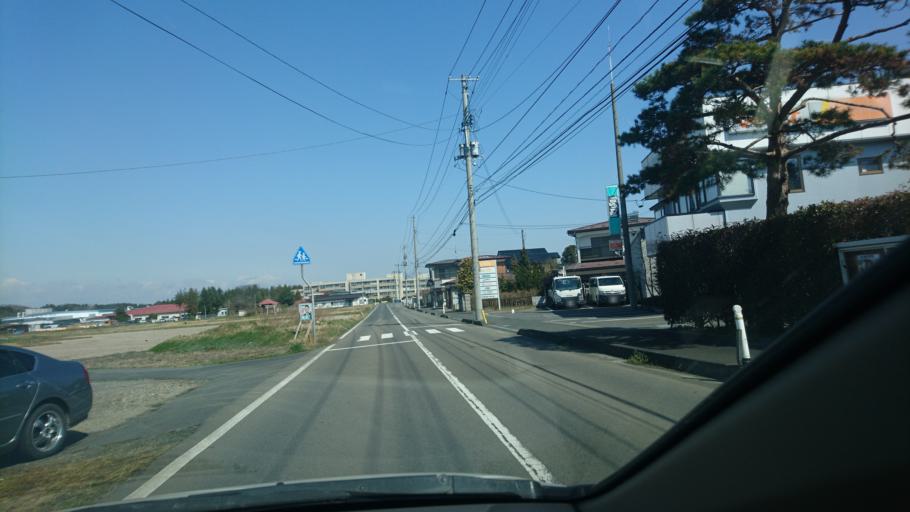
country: JP
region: Iwate
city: Mizusawa
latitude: 39.1113
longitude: 141.1554
